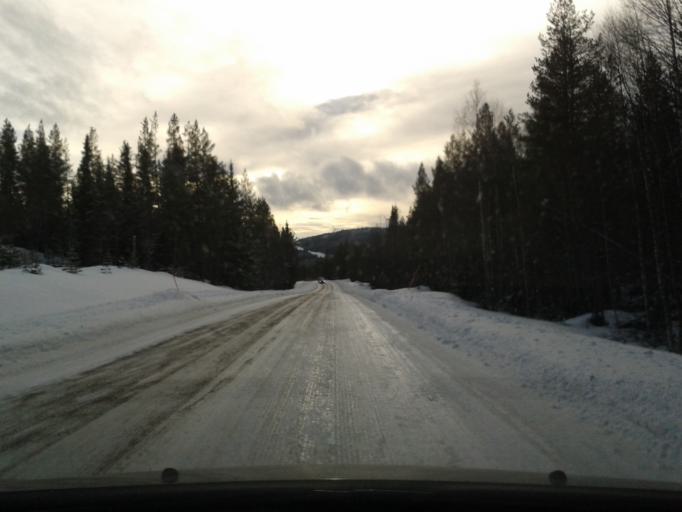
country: SE
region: Vaesterbotten
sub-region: Asele Kommun
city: Asele
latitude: 64.2636
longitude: 17.2728
